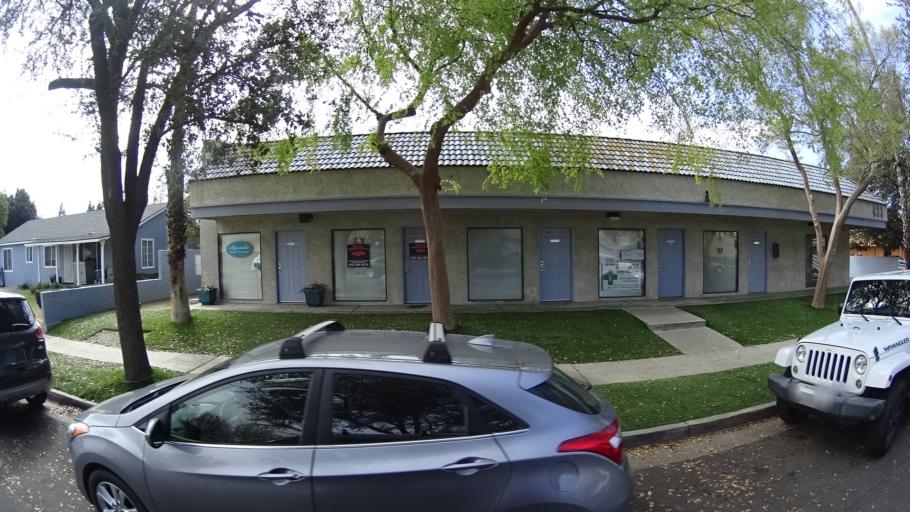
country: US
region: California
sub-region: Fresno County
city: Fresno
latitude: 36.8104
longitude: -119.7806
